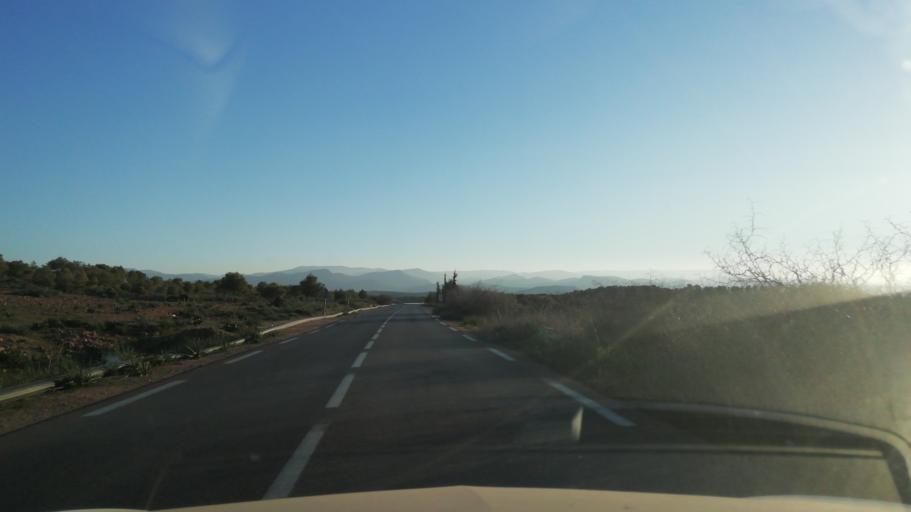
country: DZ
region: Tlemcen
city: Beni Mester
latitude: 34.8192
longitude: -1.6146
